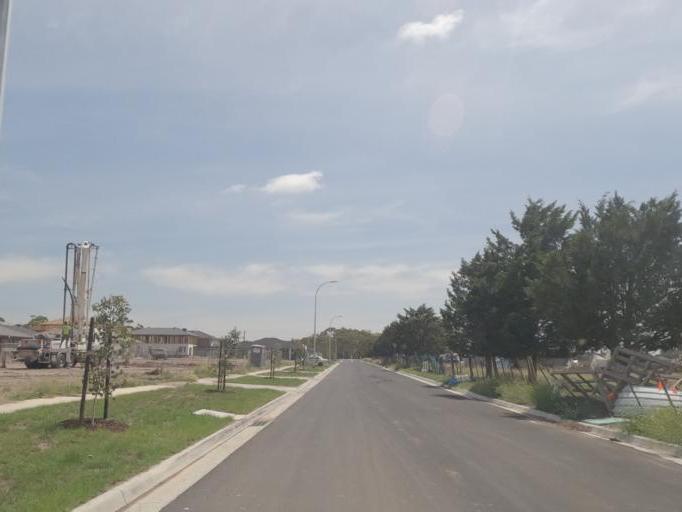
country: AU
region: Victoria
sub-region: Hume
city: Greenvale
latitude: -37.6364
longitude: 144.8755
